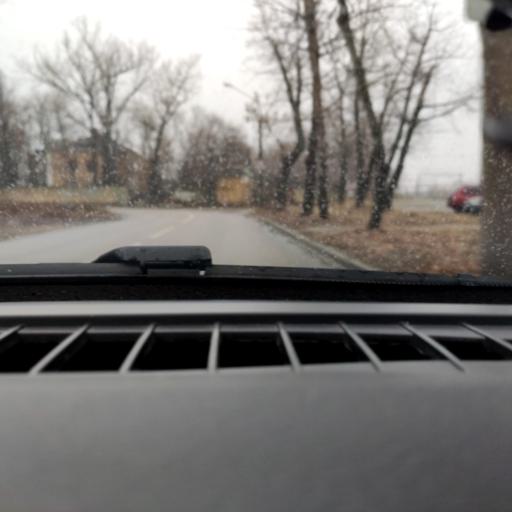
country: RU
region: Voronezj
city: Somovo
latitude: 51.7313
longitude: 39.2783
